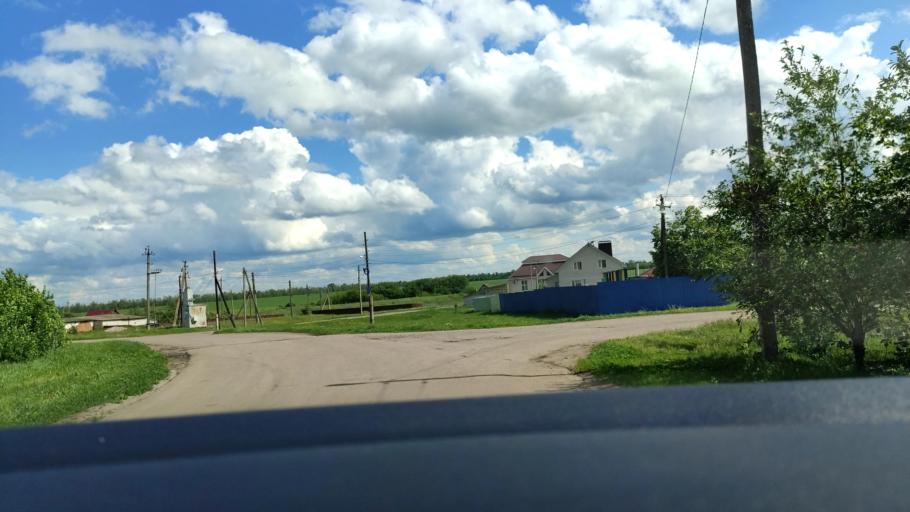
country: RU
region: Voronezj
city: Maslovka
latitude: 51.5014
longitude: 39.2948
